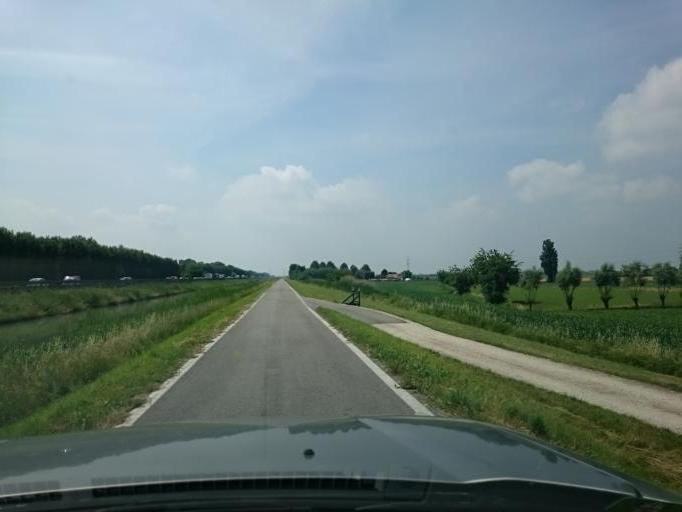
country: IT
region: Veneto
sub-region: Provincia di Padova
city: Codevigo
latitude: 45.2855
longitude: 12.1295
